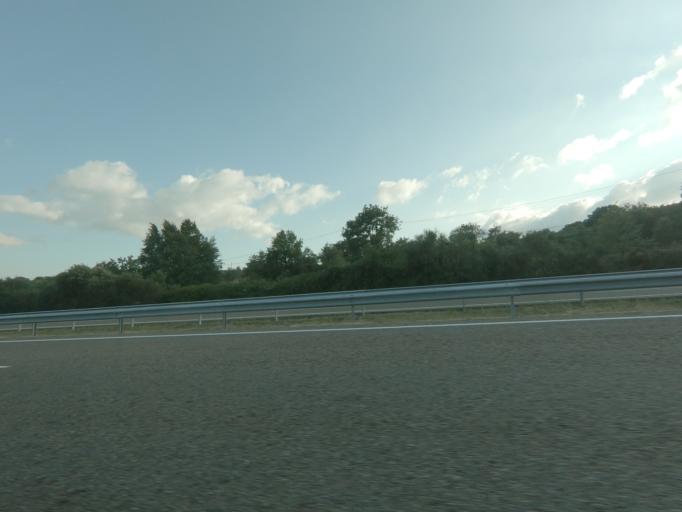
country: ES
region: Galicia
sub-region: Provincia de Ourense
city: Cualedro
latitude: 41.9912
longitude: -7.5569
